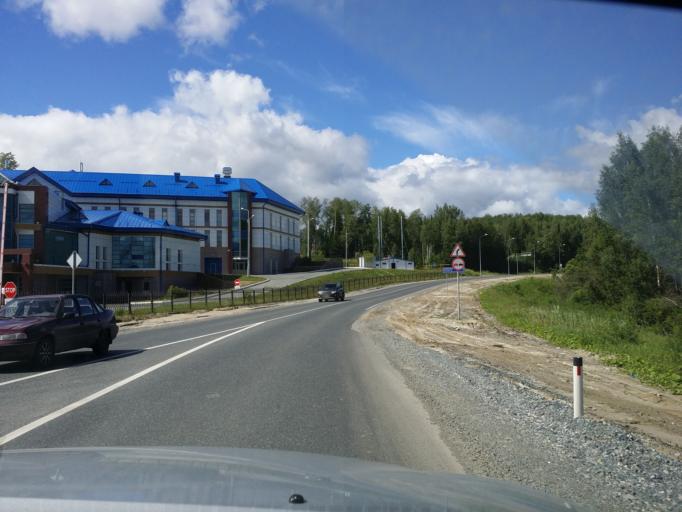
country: RU
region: Tjumen
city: Uvat
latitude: 59.1376
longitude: 68.9907
